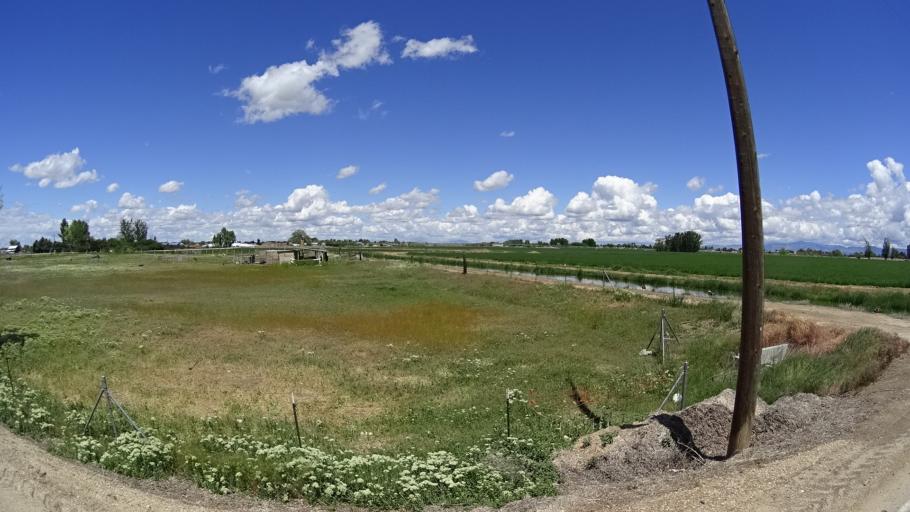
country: US
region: Idaho
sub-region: Ada County
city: Kuna
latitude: 43.5465
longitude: -116.4514
